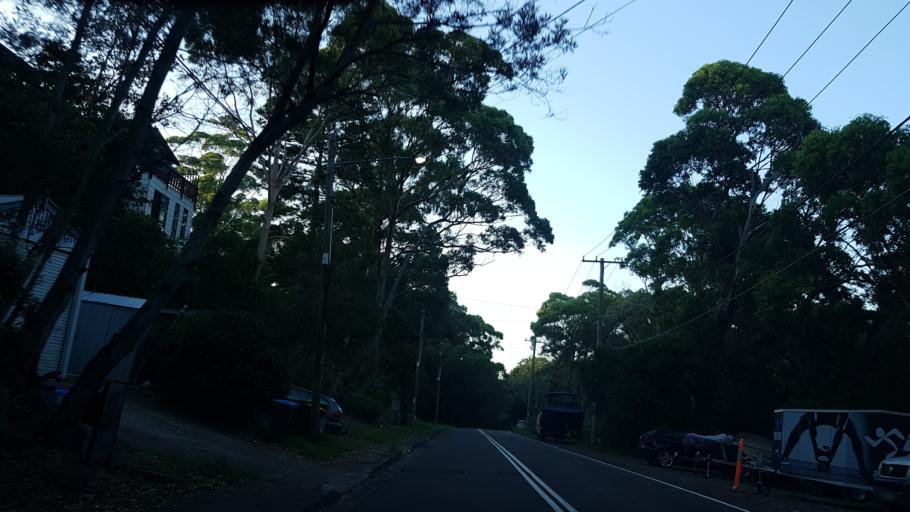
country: AU
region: New South Wales
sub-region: Warringah
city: Narrabeen
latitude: -33.7256
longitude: 151.2769
